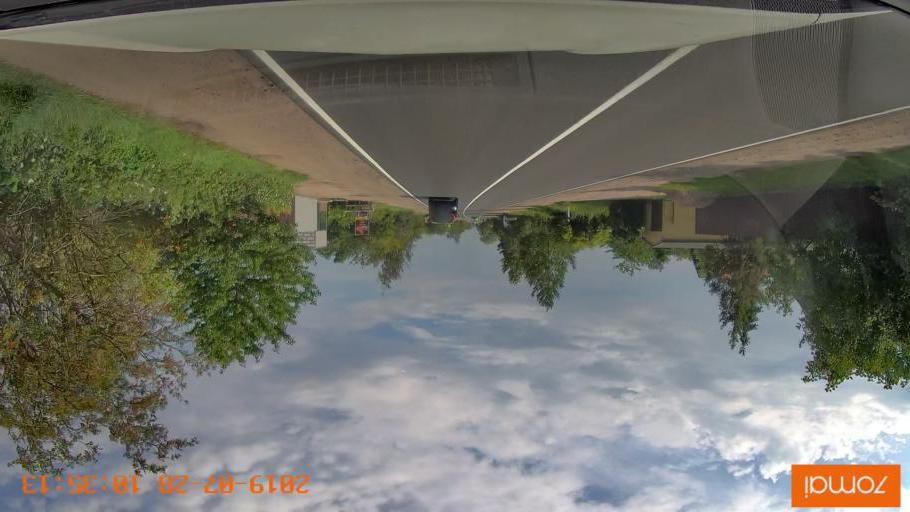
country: RU
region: Kaliningrad
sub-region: Gorod Kaliningrad
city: Kaliningrad
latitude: 54.7487
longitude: 20.4335
